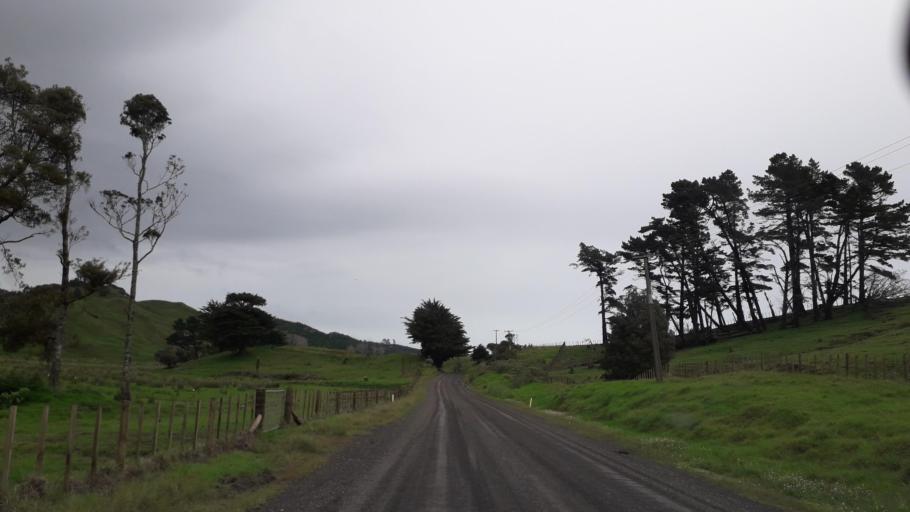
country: NZ
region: Northland
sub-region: Far North District
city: Ahipara
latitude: -35.4178
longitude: 173.3631
